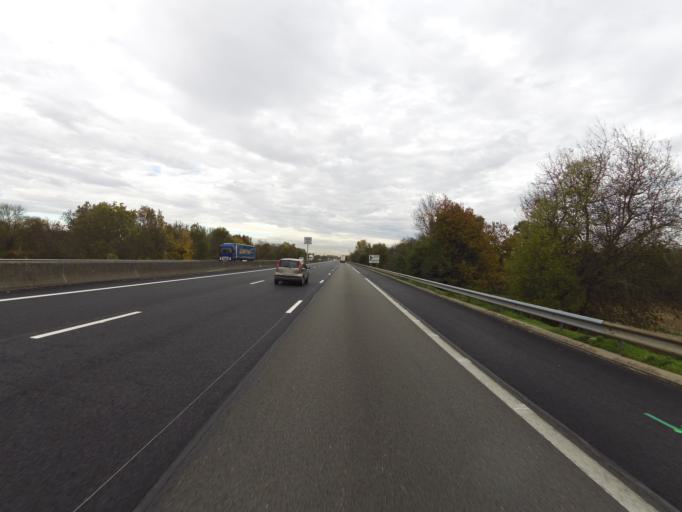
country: FR
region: Rhone-Alpes
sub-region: Departement du Rhone
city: Belleville
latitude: 46.0786
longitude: 4.7425
